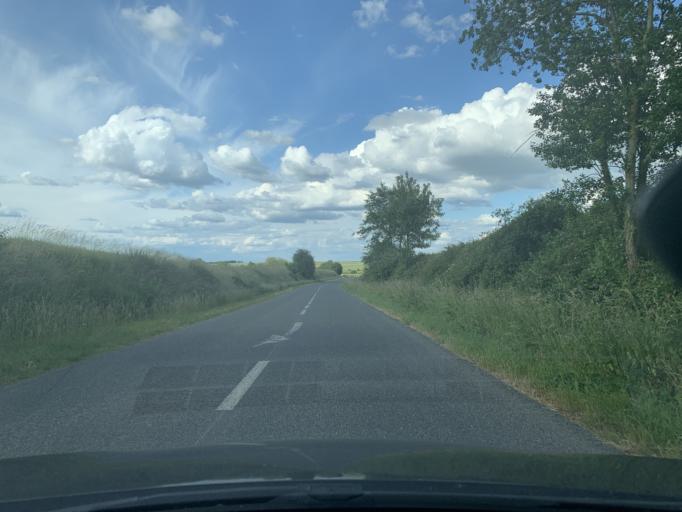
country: FR
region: Nord-Pas-de-Calais
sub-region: Departement du Nord
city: Gouzeaucourt
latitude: 50.0617
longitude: 3.1294
